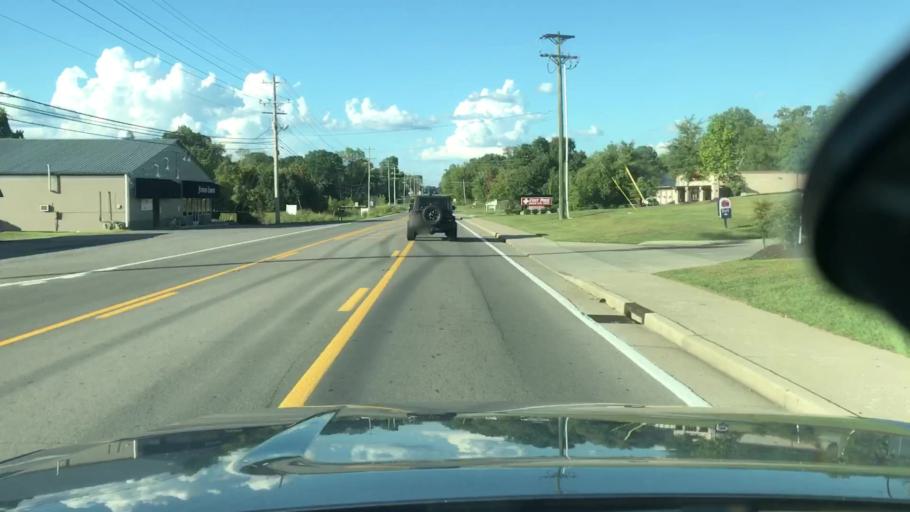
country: US
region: Tennessee
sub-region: Williamson County
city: Fairview
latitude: 35.9626
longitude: -87.1353
